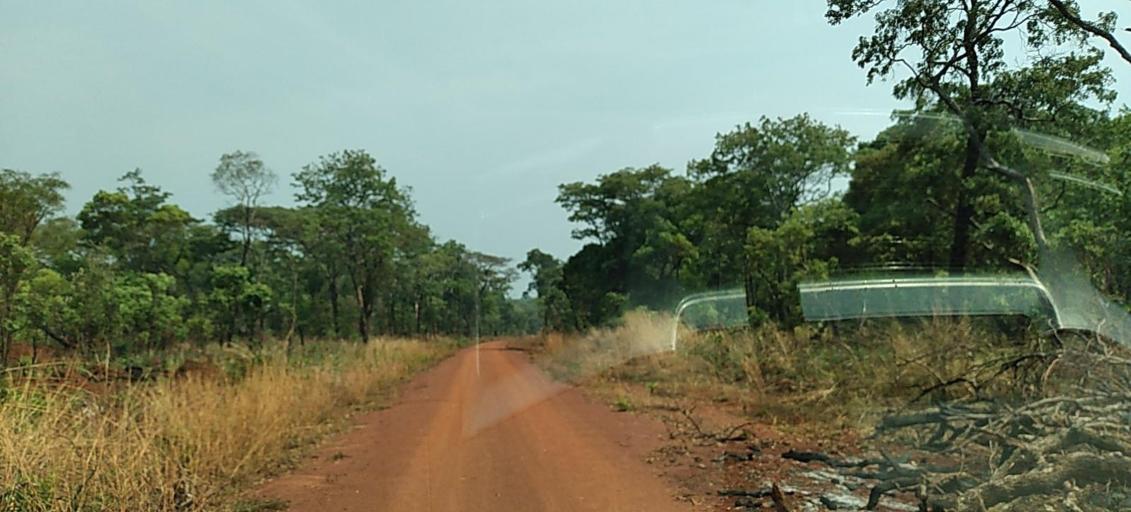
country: ZM
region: North-Western
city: Kansanshi
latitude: -12.0004
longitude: 26.8405
